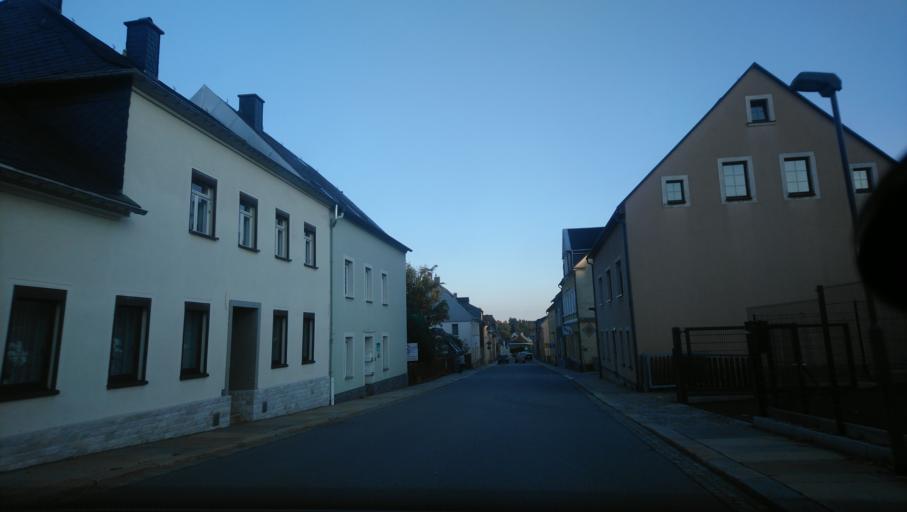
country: DE
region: Saxony
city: Geyer
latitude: 50.6282
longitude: 12.9176
